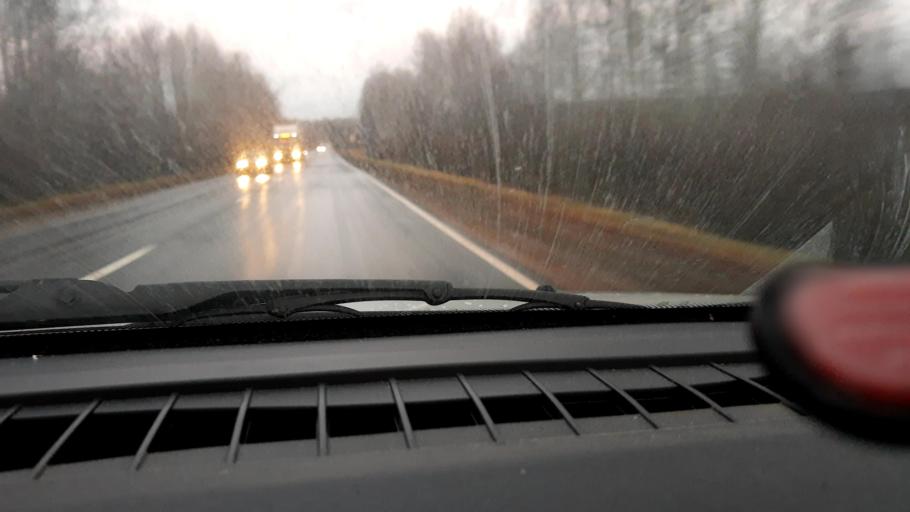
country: RU
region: Nizjnij Novgorod
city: Uren'
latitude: 57.2454
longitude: 45.5883
